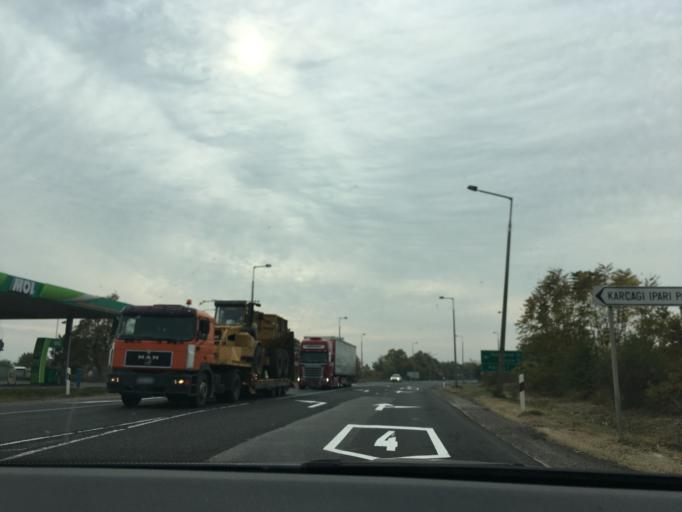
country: HU
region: Jasz-Nagykun-Szolnok
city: Karcag
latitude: 47.2969
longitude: 20.9312
